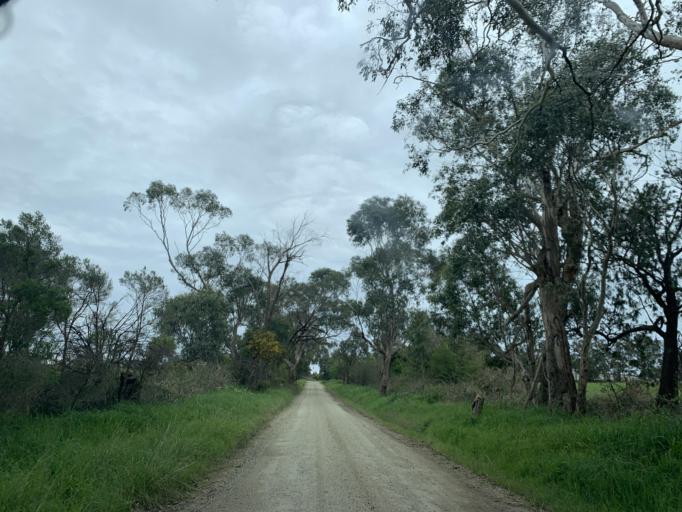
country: AU
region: Victoria
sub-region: Cardinia
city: Garfield
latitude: -38.1038
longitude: 145.6473
